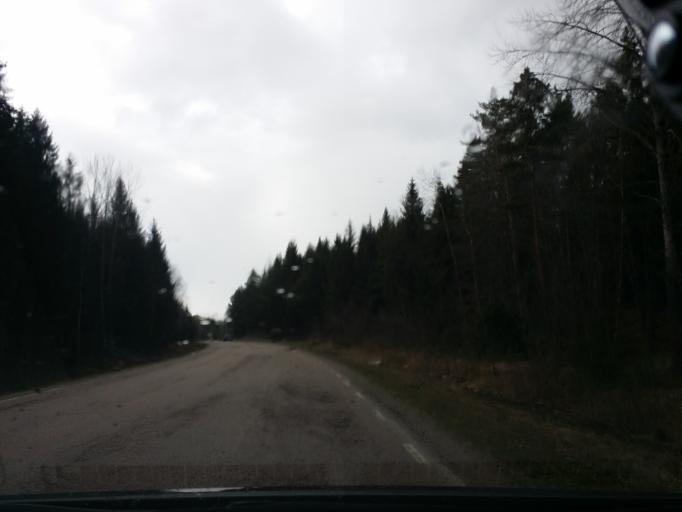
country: SE
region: Uppsala
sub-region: Enkopings Kommun
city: Enkoping
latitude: 59.6348
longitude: 17.1441
